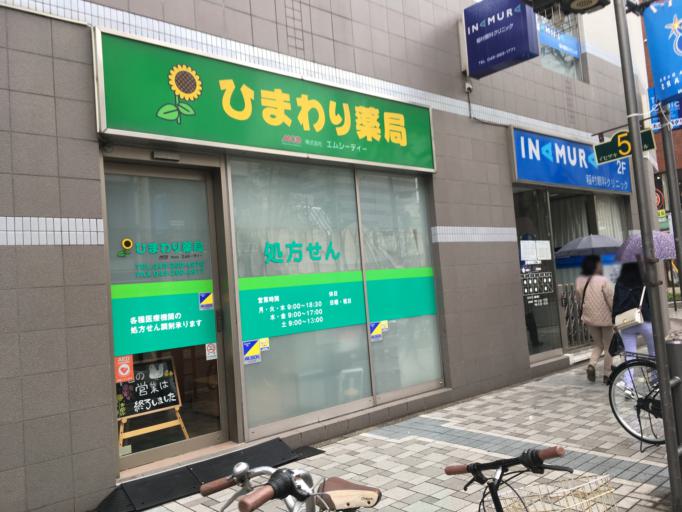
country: JP
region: Kanagawa
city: Yokohama
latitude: 35.4408
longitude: 139.6279
